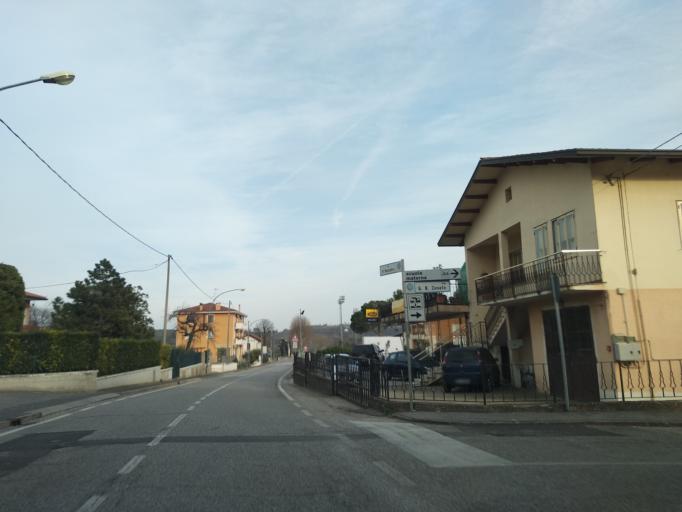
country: IT
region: Veneto
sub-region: Provincia di Vicenza
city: Barbarano Vicentino
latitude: 45.4091
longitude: 11.5443
